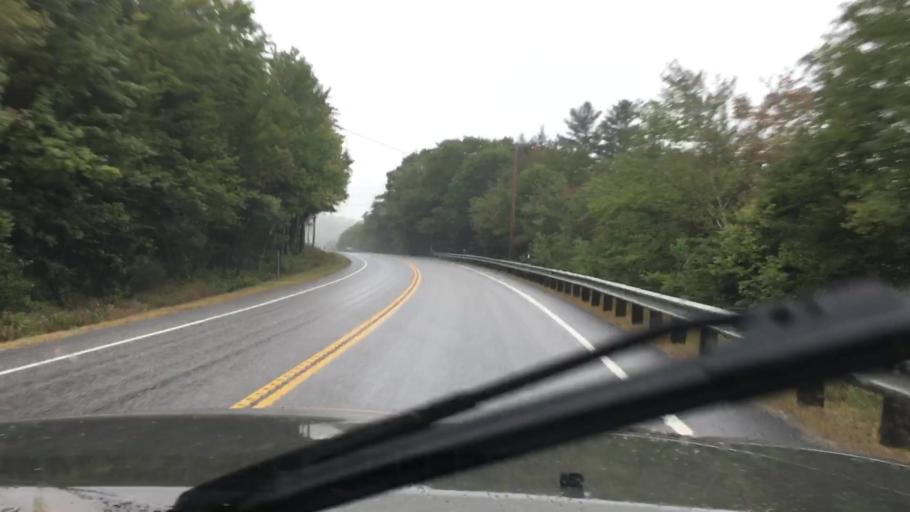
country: US
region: New Hampshire
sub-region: Cheshire County
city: Harrisville
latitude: 43.0302
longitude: -72.1198
